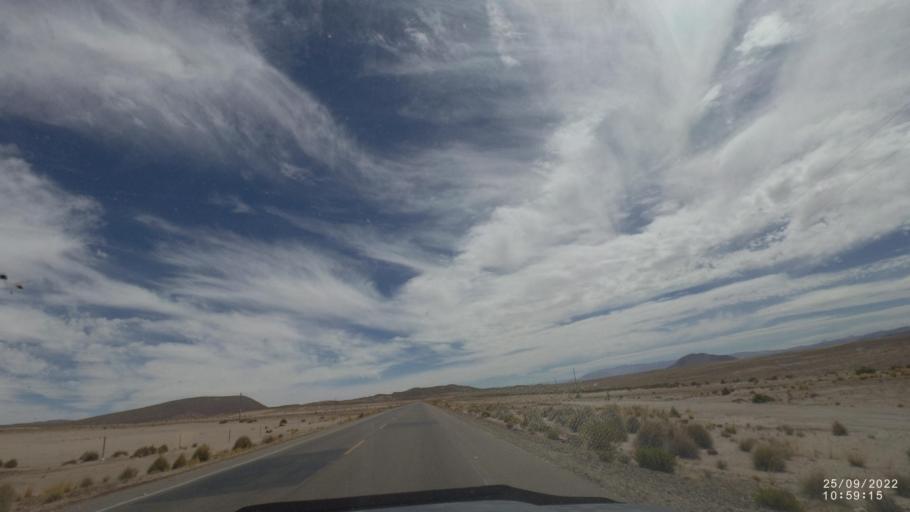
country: BO
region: Oruro
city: Challapata
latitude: -19.4518
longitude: -66.9094
